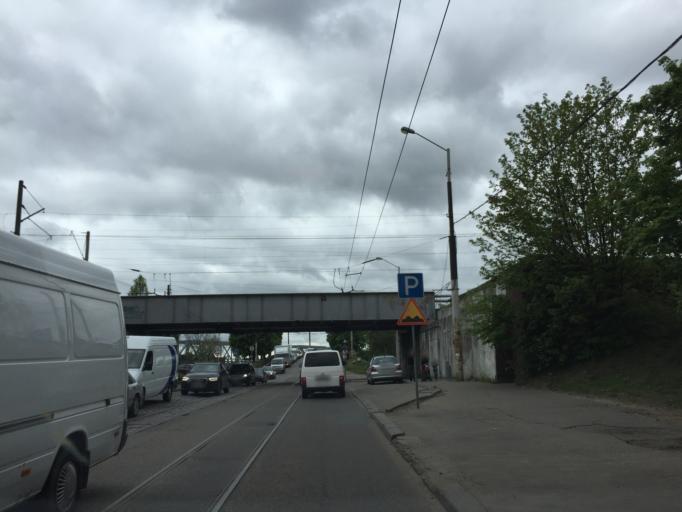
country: RU
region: Kaliningrad
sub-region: Gorod Kaliningrad
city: Kaliningrad
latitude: 54.6968
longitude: 20.4934
